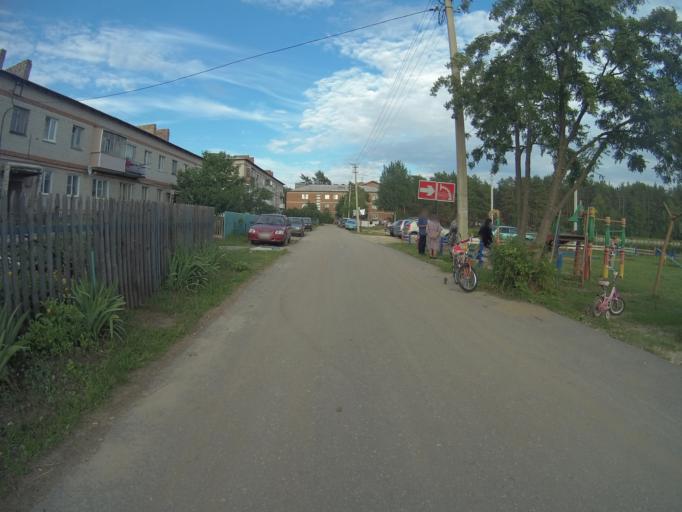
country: RU
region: Vladimir
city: Kommunar
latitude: 56.1214
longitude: 40.4588
